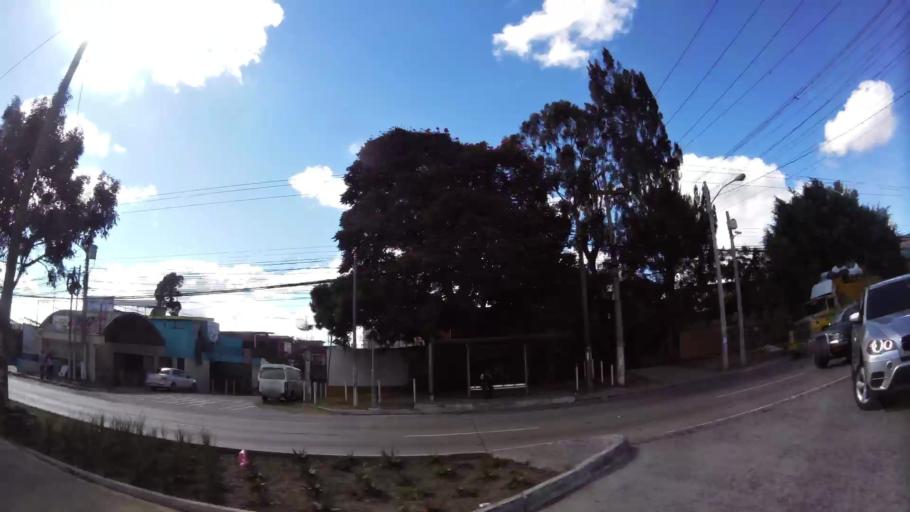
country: GT
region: Guatemala
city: Santa Catarina Pinula
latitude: 14.5810
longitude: -90.5461
